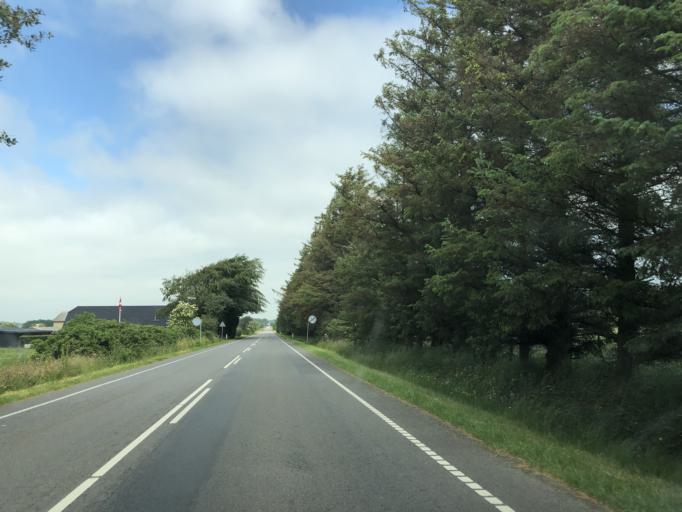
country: DK
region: South Denmark
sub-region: Varde Kommune
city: Varde
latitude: 55.6626
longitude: 8.4900
